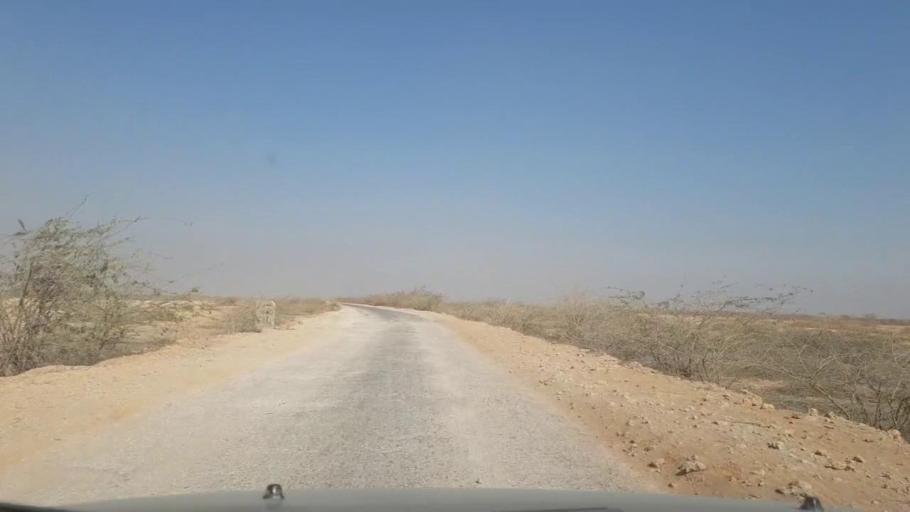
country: PK
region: Sindh
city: Thatta
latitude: 24.8489
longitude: 67.8935
